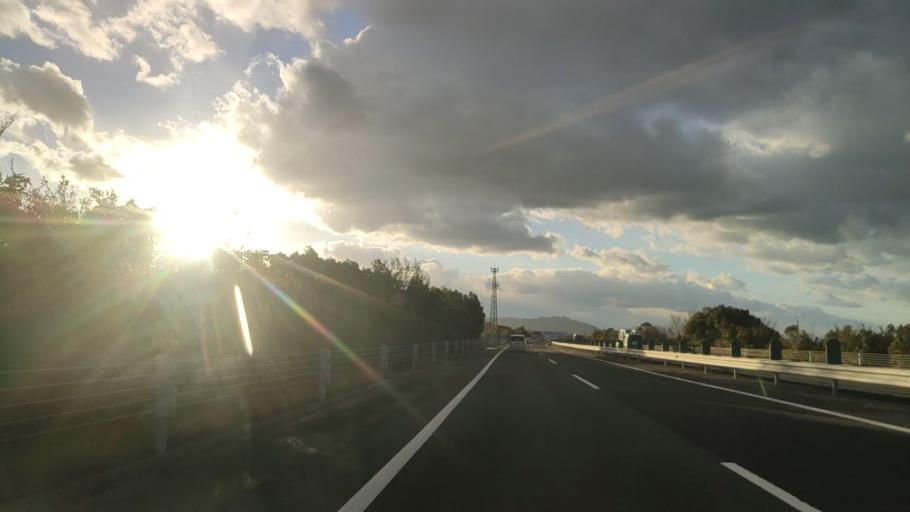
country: JP
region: Ehime
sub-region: Shikoku-chuo Shi
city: Matsuyama
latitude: 33.7851
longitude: 132.8536
